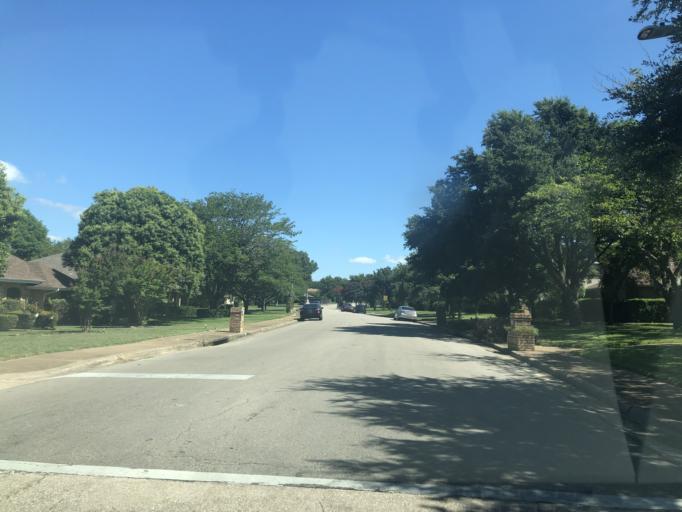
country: US
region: Texas
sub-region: Dallas County
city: Duncanville
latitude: 32.6422
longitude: -96.9335
